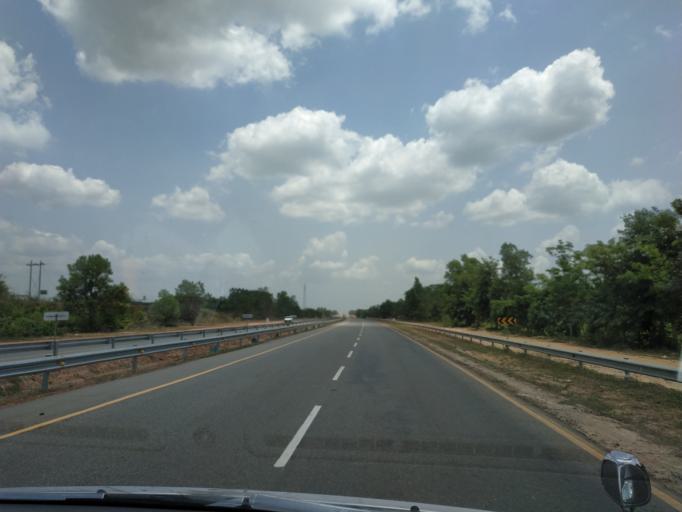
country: MM
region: Bago
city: Thanatpin
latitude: 17.2975
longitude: 96.2272
